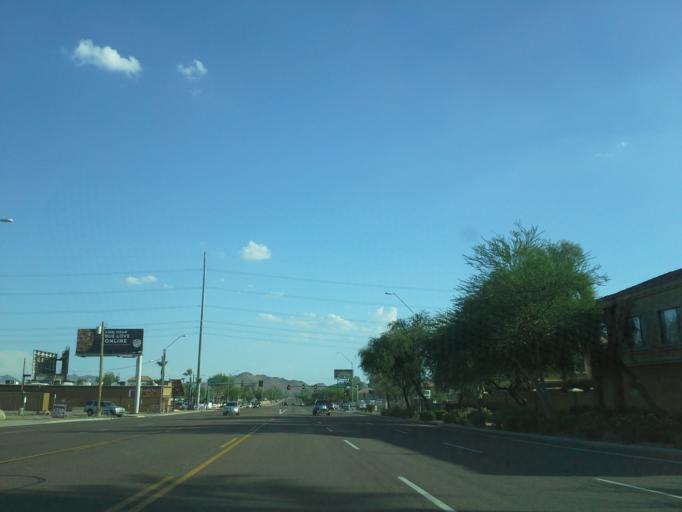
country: US
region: Arizona
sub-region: Maricopa County
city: Paradise Valley
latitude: 33.6568
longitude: -112.0309
